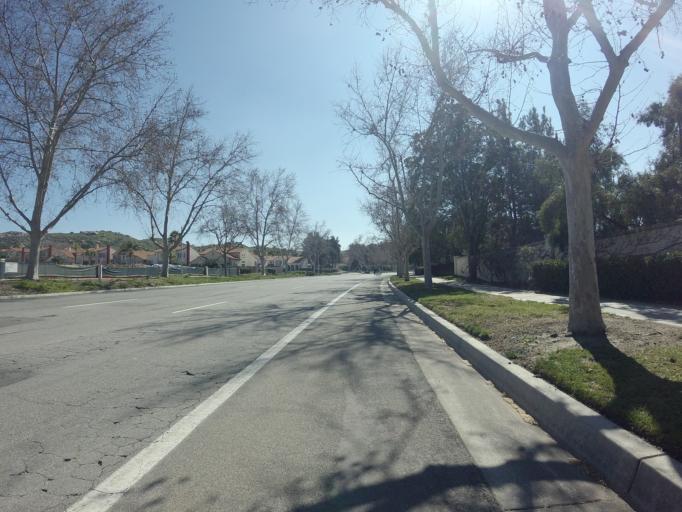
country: US
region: California
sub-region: Riverside County
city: Moreno Valley
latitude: 33.9004
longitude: -117.1742
